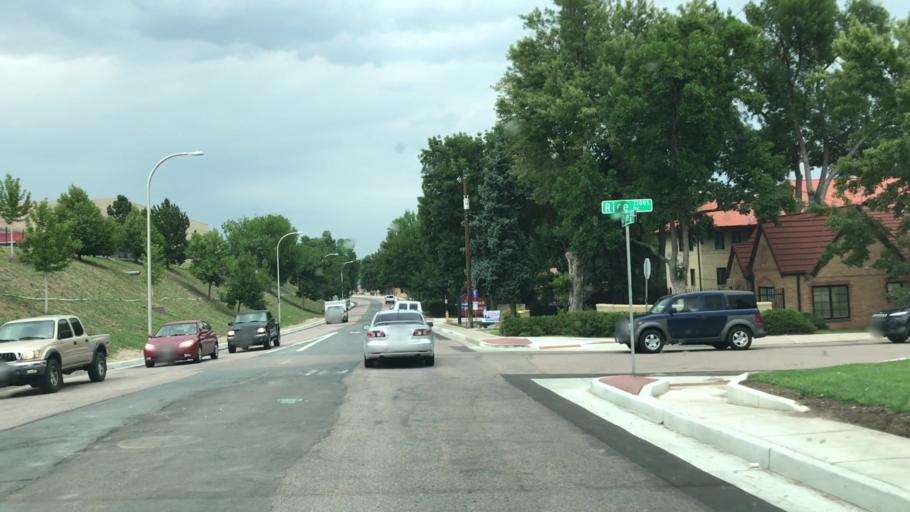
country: US
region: Colorado
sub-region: El Paso County
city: Colorado Springs
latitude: 38.8006
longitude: -104.8175
